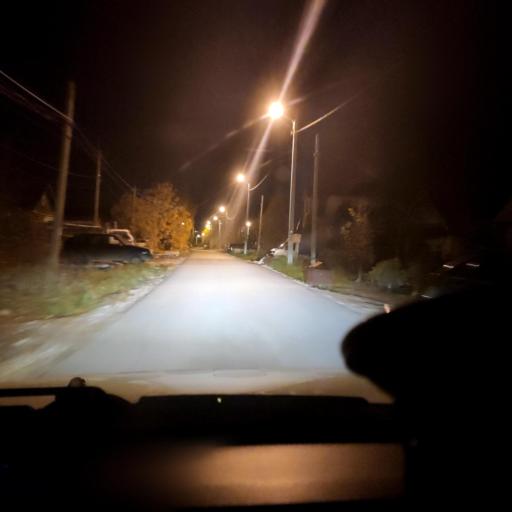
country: RU
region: Perm
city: Perm
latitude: 57.9808
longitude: 56.3094
